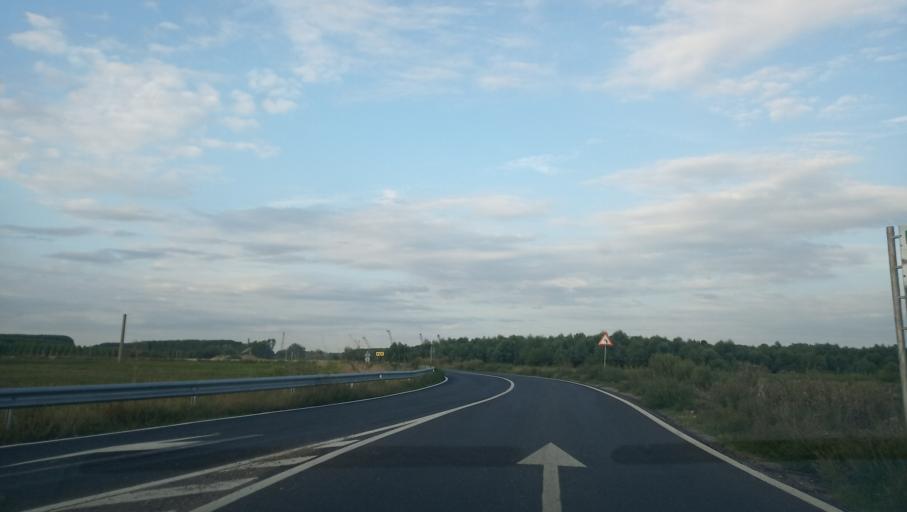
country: RO
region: Calarasi
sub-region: Municipiul Calarasi
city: Calarasi
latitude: 44.1638
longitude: 27.3134
